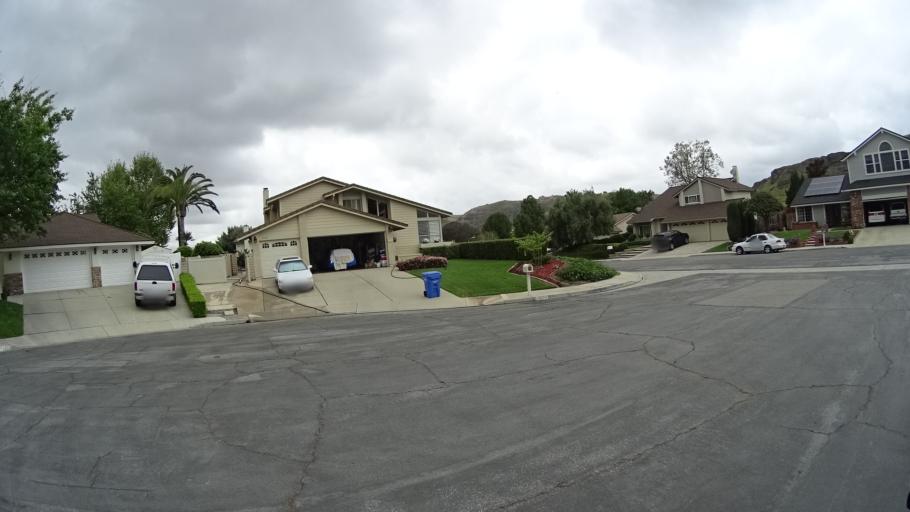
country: US
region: California
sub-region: Ventura County
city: Moorpark
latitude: 34.2216
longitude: -118.8898
